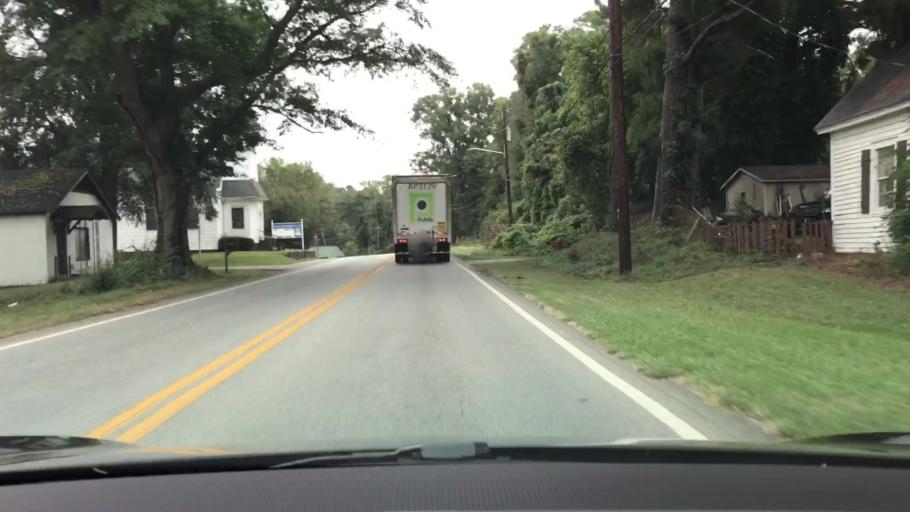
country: US
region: Georgia
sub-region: Greene County
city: Greensboro
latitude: 33.5799
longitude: -83.1877
